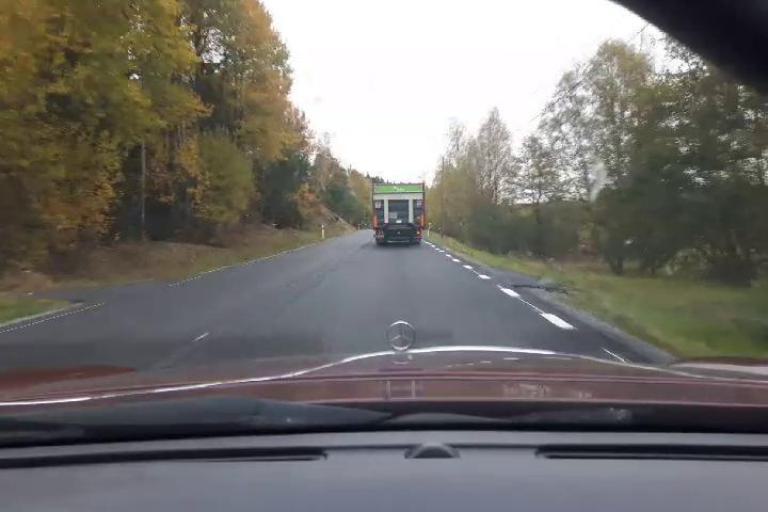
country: SE
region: Soedermanland
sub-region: Strangnas Kommun
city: Strangnas
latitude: 59.4345
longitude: 17.0227
